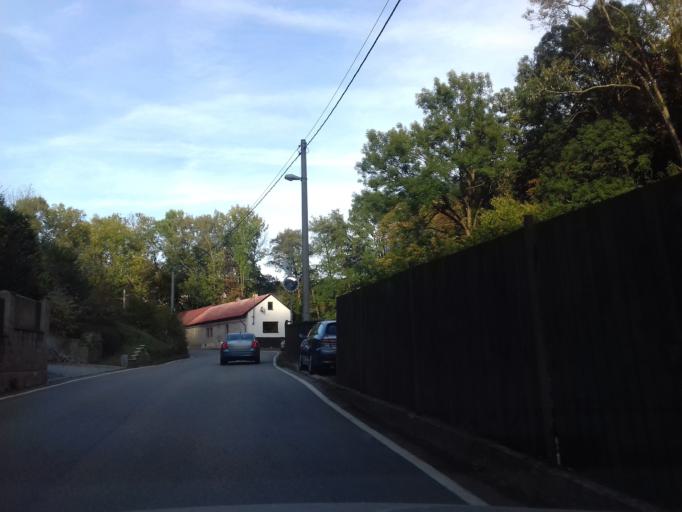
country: CZ
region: Central Bohemia
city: Kamenny Privoz
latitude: 49.8770
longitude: 14.5020
